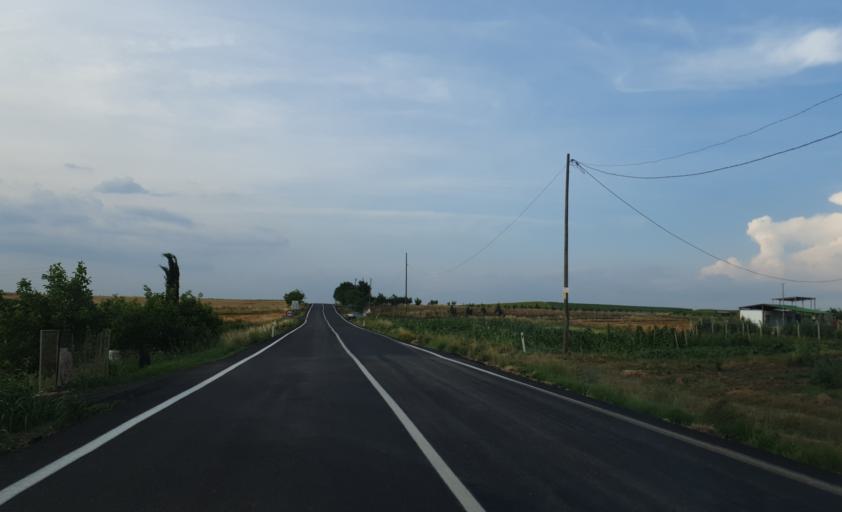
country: TR
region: Tekirdag
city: Hayrabolu
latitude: 41.2941
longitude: 27.1349
